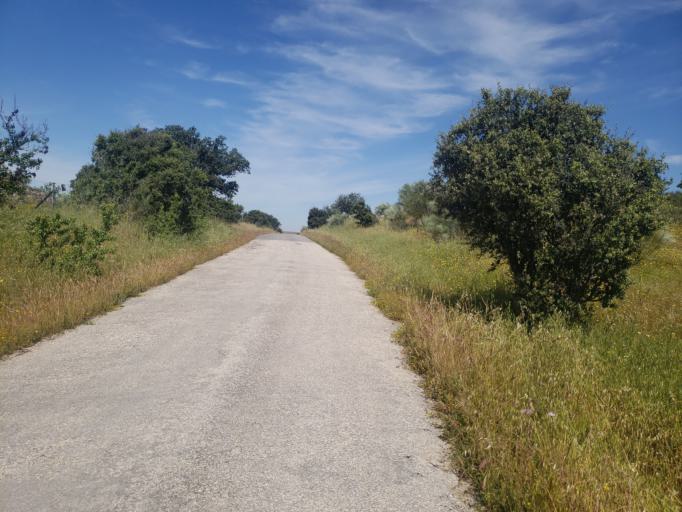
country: ES
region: Extremadura
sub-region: Provincia de Caceres
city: Malpartida de Caceres
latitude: 39.4174
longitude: -6.5021
